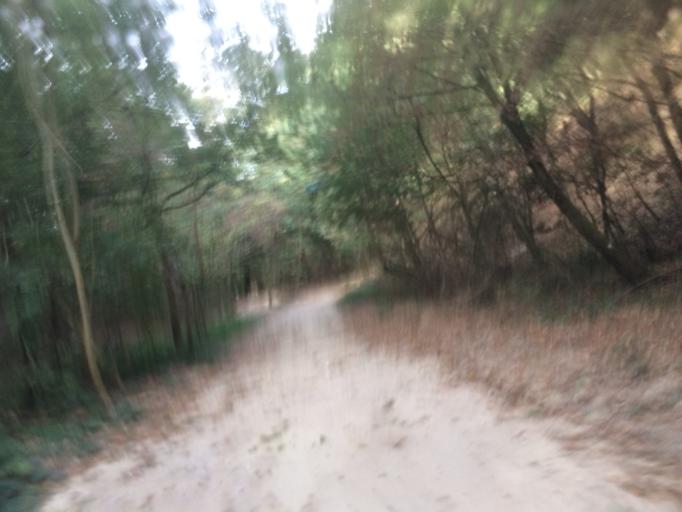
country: FR
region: Ile-de-France
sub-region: Departement des Yvelines
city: Bonnelles
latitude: 48.6268
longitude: 2.0266
